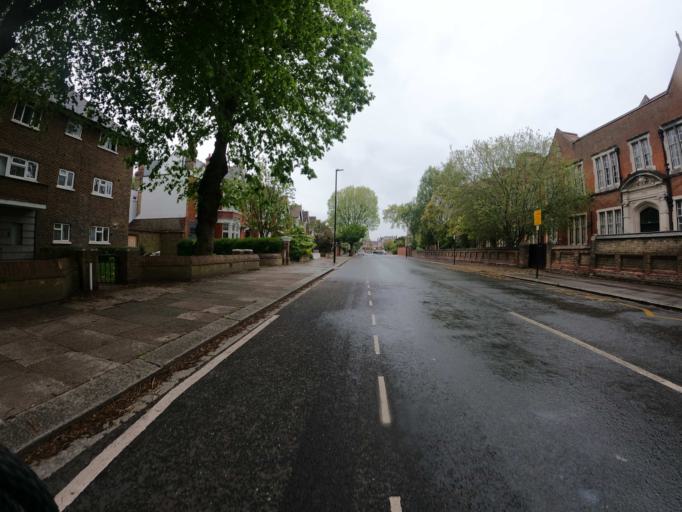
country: GB
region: England
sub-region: Greater London
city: Acton
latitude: 51.5134
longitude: -0.2800
